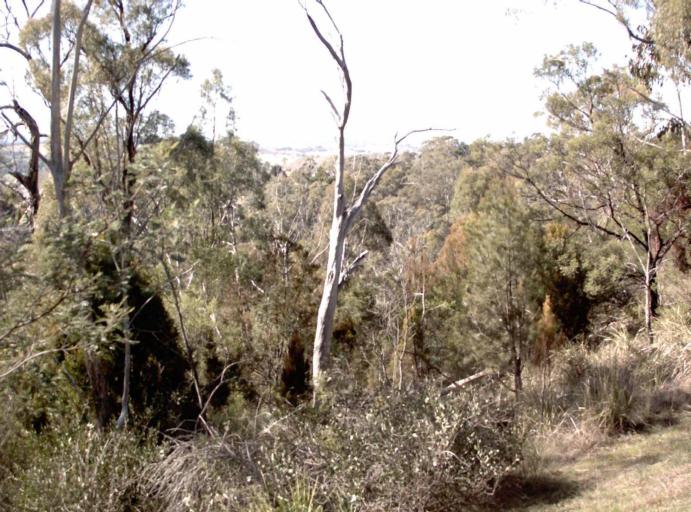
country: AU
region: Tasmania
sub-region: Launceston
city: Newstead
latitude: -41.4560
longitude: 147.1657
